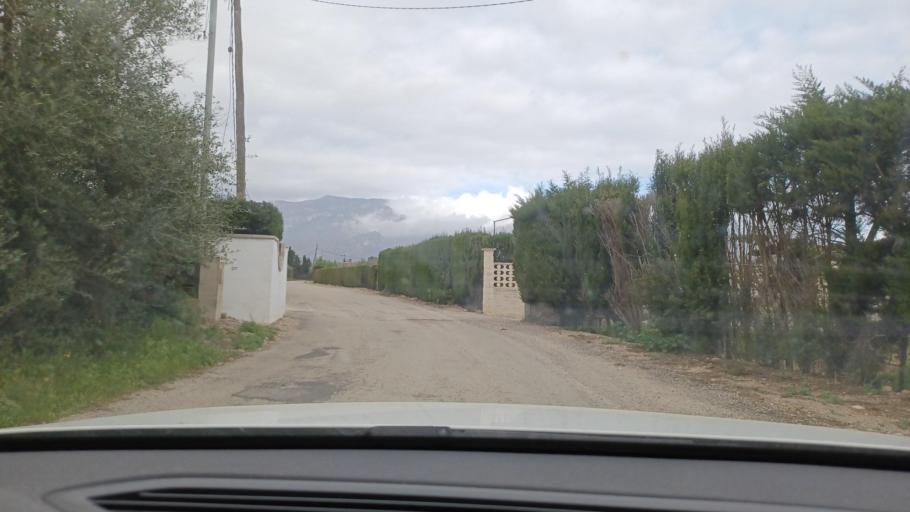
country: ES
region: Catalonia
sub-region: Provincia de Tarragona
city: Tortosa
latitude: 40.7923
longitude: 0.4647
